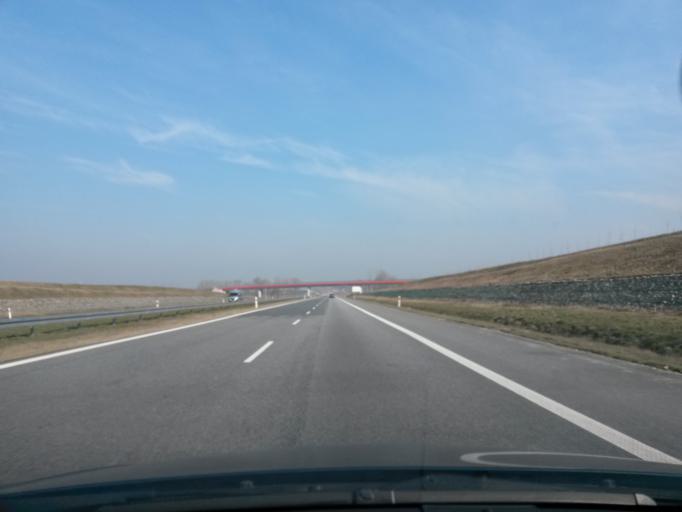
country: PL
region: Lodz Voivodeship
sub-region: Powiat kutnowski
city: Krzyzanow
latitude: 52.1665
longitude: 19.4844
